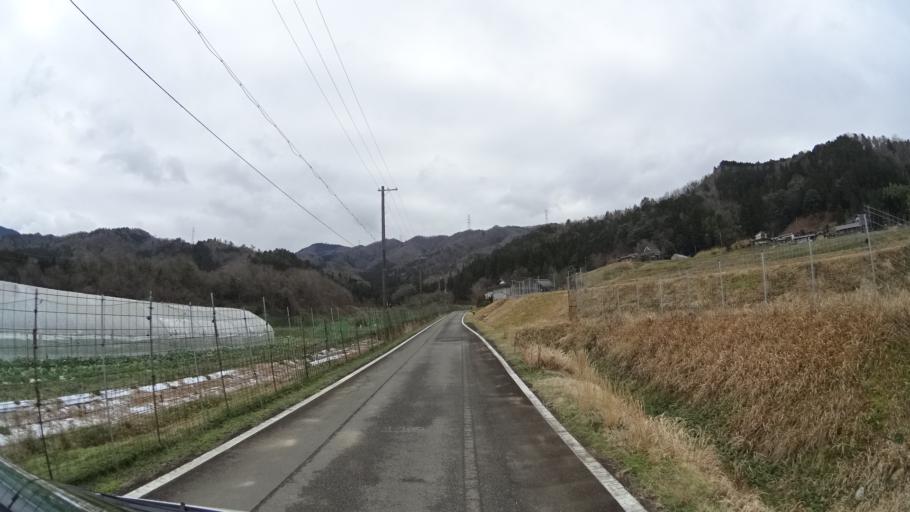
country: JP
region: Kyoto
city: Ayabe
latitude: 35.3230
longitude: 135.3593
